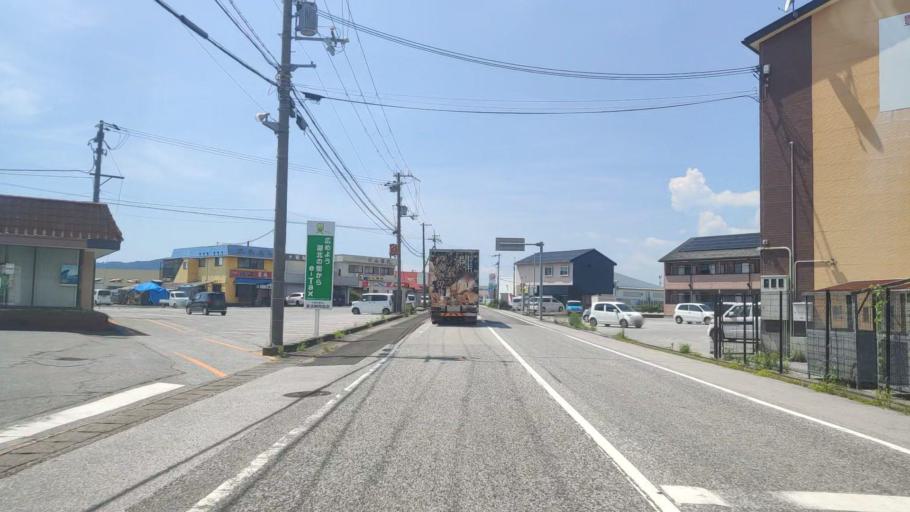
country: JP
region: Shiga Prefecture
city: Nagahama
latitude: 35.3857
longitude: 136.3656
